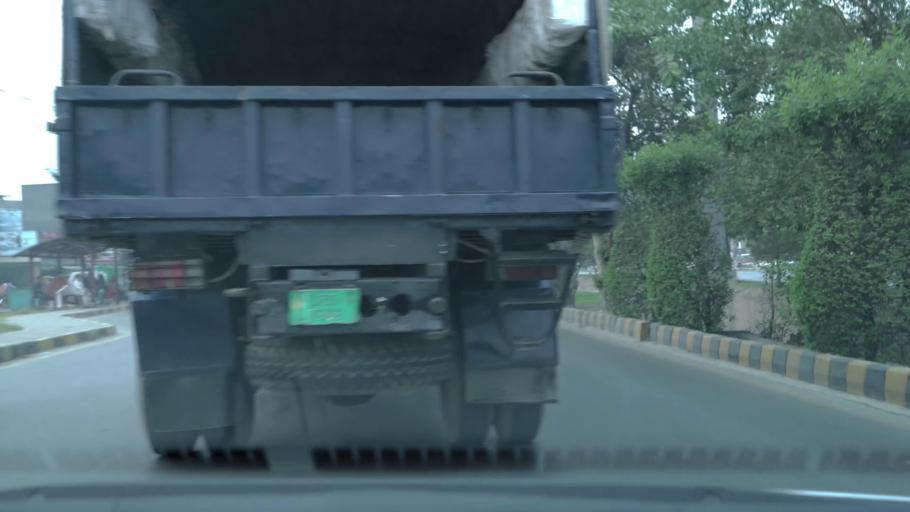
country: PK
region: Punjab
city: Lahore
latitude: 31.4781
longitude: 74.3009
